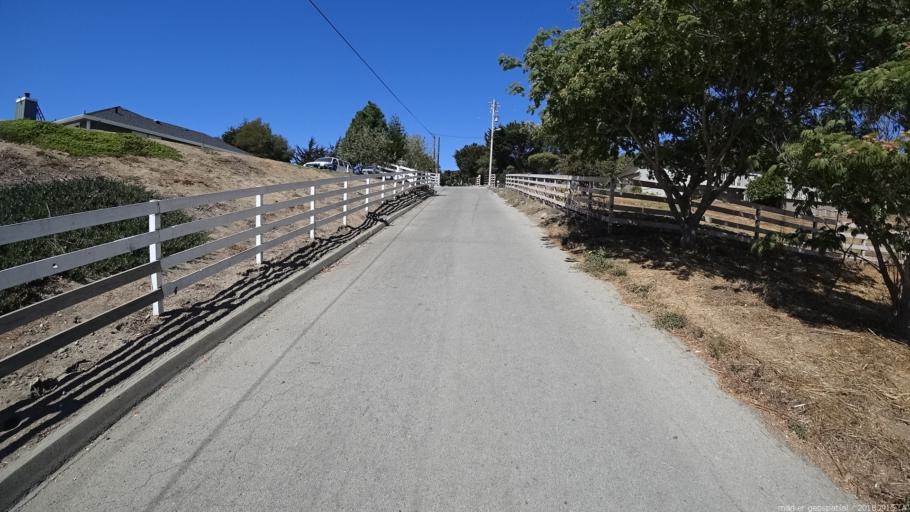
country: US
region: California
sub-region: Monterey County
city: Las Lomas
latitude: 36.8669
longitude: -121.7521
